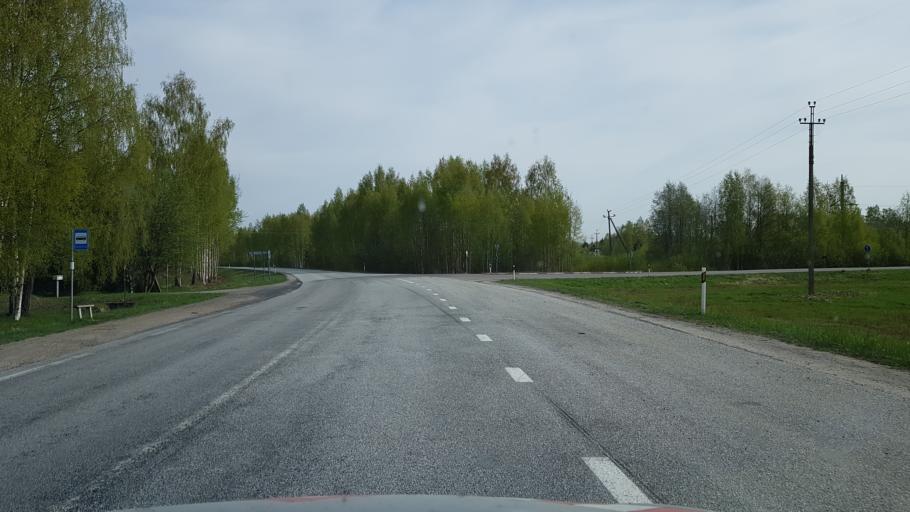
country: EE
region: Paernumaa
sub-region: Audru vald
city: Audru
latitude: 58.4054
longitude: 24.3058
